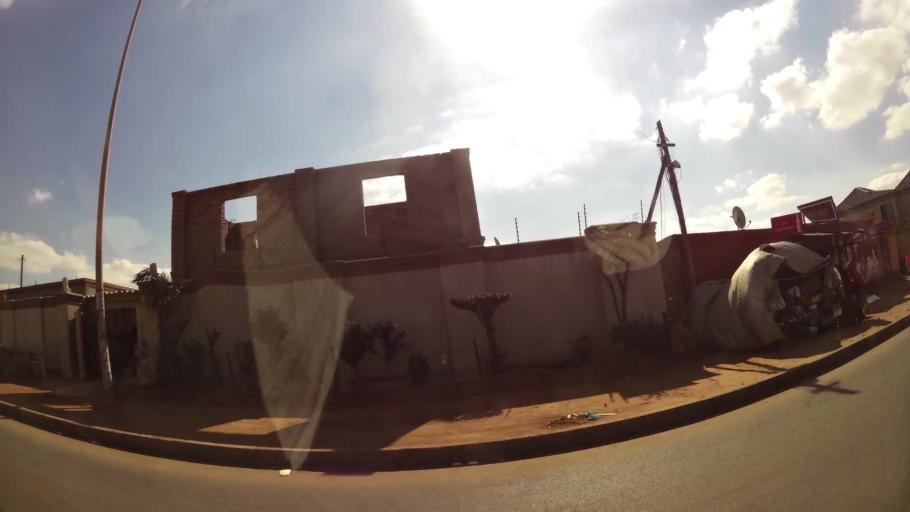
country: ZA
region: Gauteng
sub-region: Ekurhuleni Metropolitan Municipality
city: Tembisa
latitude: -26.0127
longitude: 28.1766
